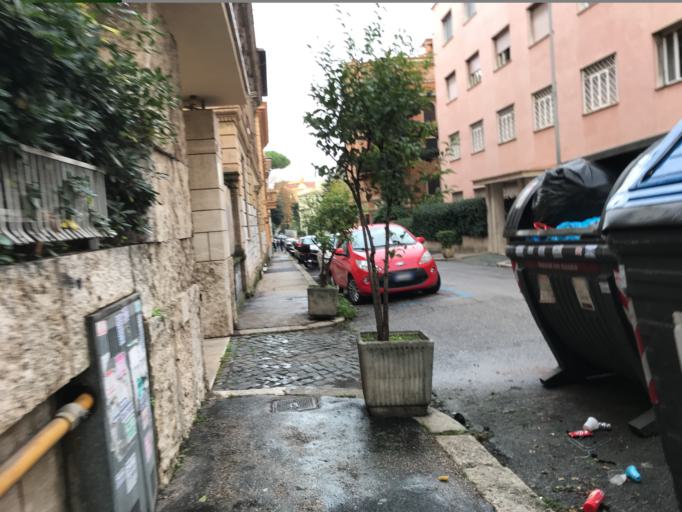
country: IT
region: Latium
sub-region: Citta metropolitana di Roma Capitale
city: Rome
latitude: 41.9156
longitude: 12.5137
